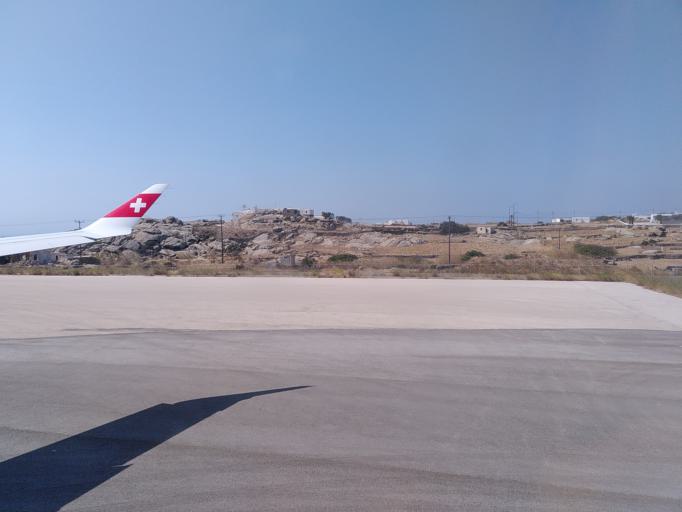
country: GR
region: South Aegean
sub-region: Nomos Kykladon
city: Mykonos
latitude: 37.4273
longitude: 25.3514
